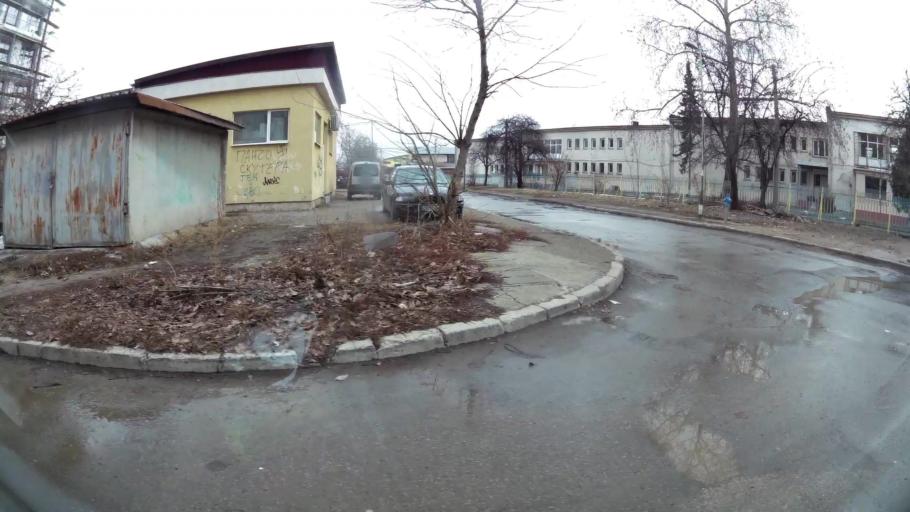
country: BG
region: Sofiya
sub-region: Obshtina Bozhurishte
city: Bozhurishte
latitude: 42.7280
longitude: 23.2563
